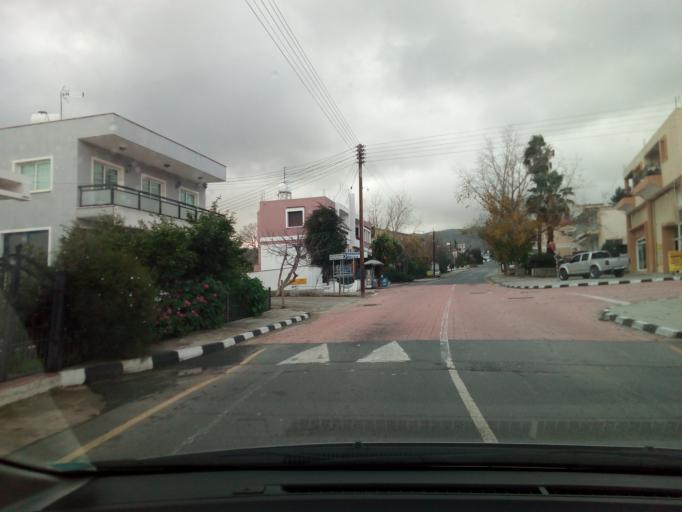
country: CY
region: Pafos
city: Tala
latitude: 34.9214
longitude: 32.4770
